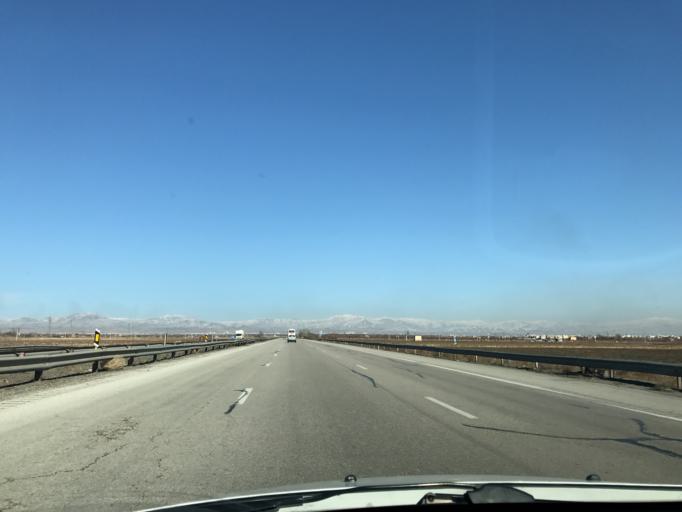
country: IR
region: Qazvin
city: Qazvin
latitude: 36.2265
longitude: 49.8924
